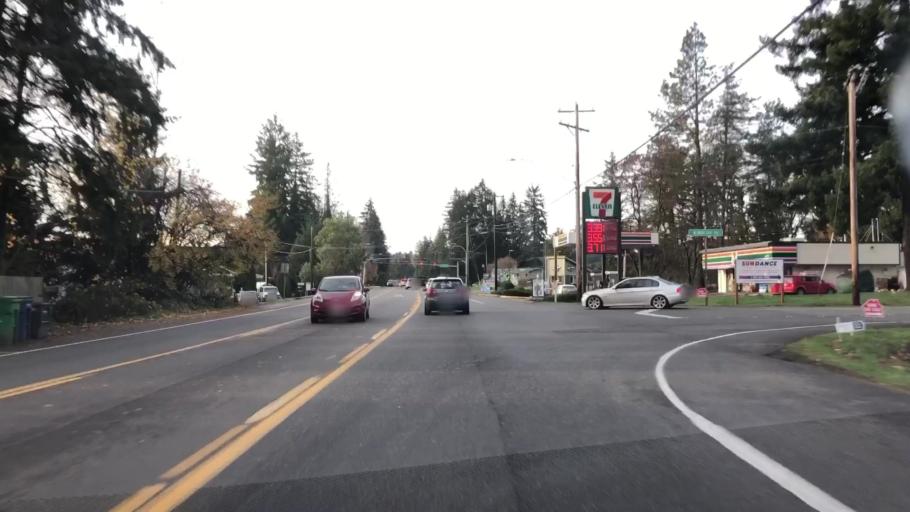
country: US
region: Washington
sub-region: Snohomish County
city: Martha Lake
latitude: 47.8233
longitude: -122.2363
